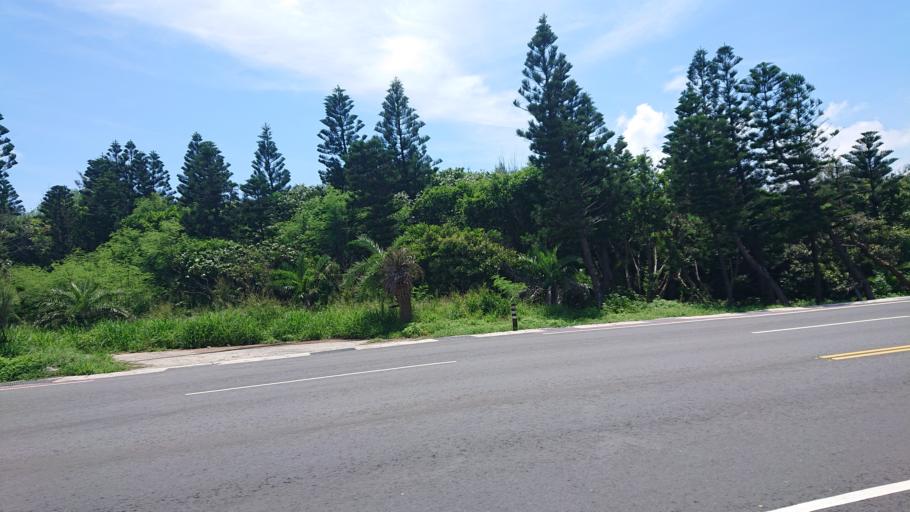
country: TW
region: Taiwan
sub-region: Penghu
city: Ma-kung
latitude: 23.6281
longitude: 119.6024
